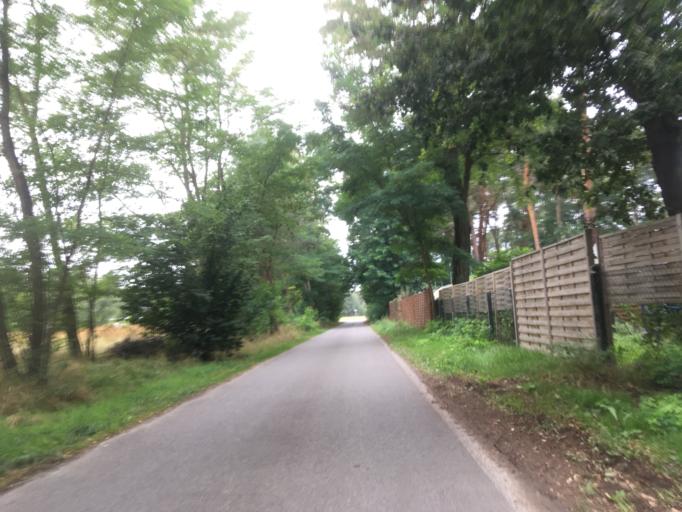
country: DE
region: Brandenburg
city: Bestensee
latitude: 52.2396
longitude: 13.7660
